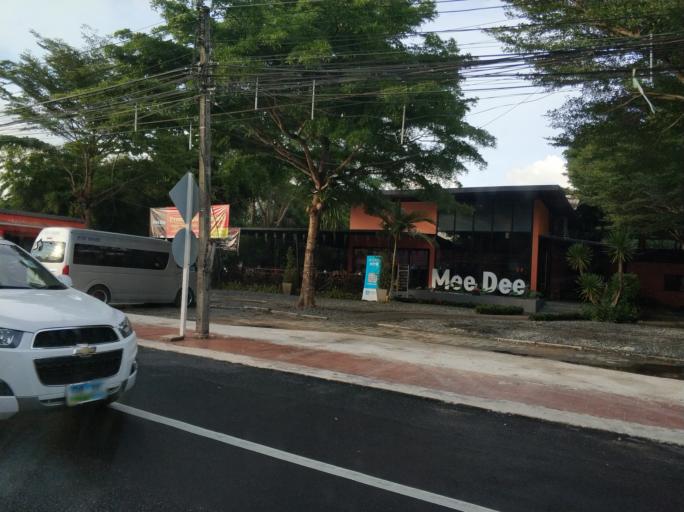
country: TH
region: Phuket
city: Kathu
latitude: 7.8992
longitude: 98.3436
